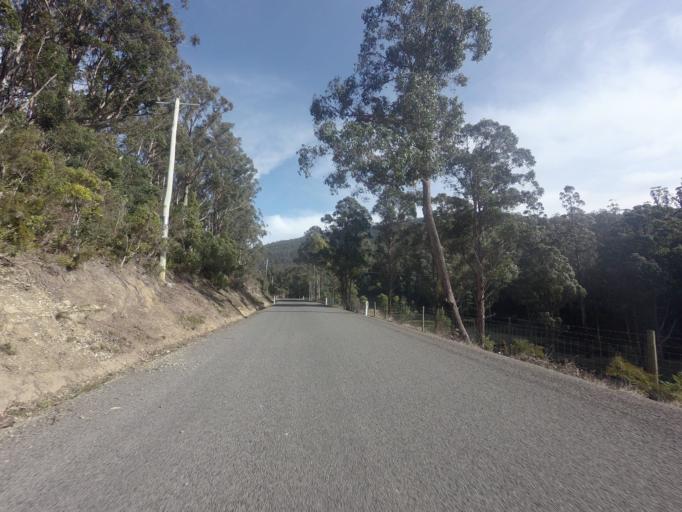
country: AU
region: Tasmania
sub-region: Huon Valley
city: Huonville
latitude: -43.0439
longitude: 147.1209
